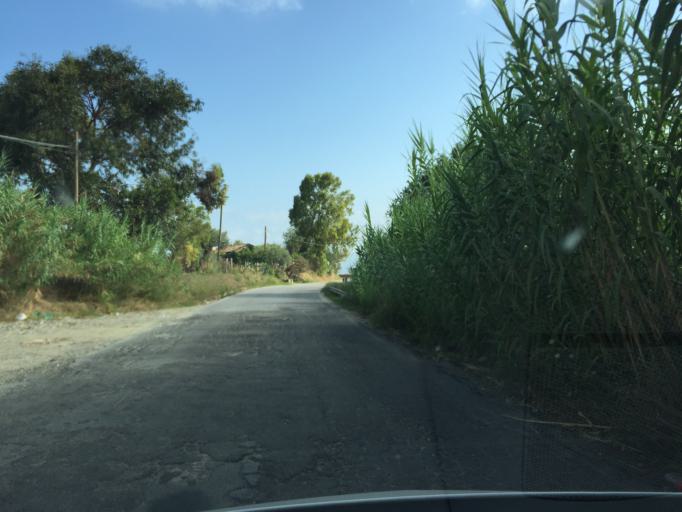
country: IT
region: Calabria
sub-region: Provincia di Vibo-Valentia
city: Pannaconi
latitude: 38.7062
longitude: 16.0500
